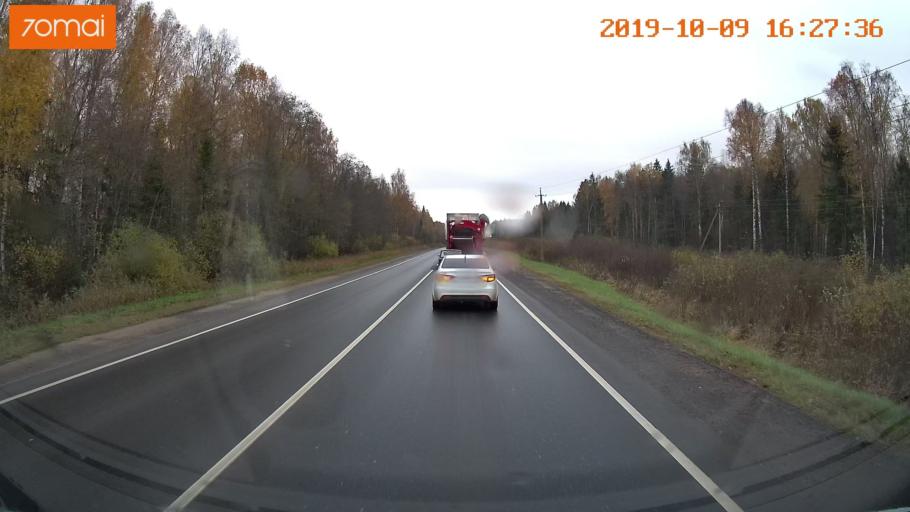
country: RU
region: Kostroma
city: Oktyabr'skiy
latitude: 57.6325
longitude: 40.9287
